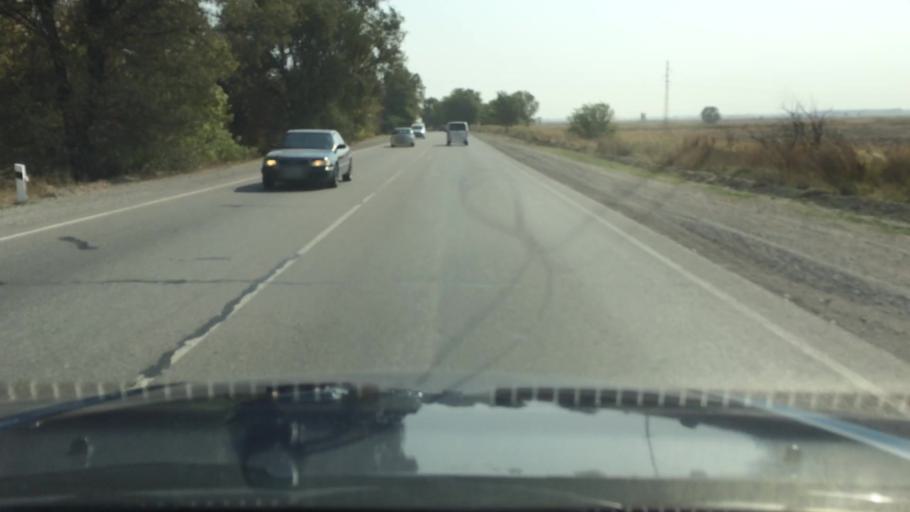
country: KG
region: Chuy
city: Lebedinovka
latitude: 42.9237
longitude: 74.7039
